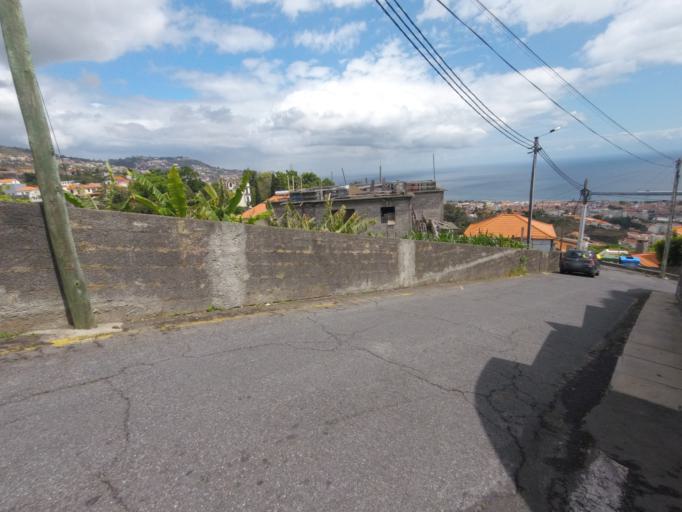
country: PT
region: Madeira
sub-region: Funchal
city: Nossa Senhora do Monte
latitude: 32.6639
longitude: -16.9129
